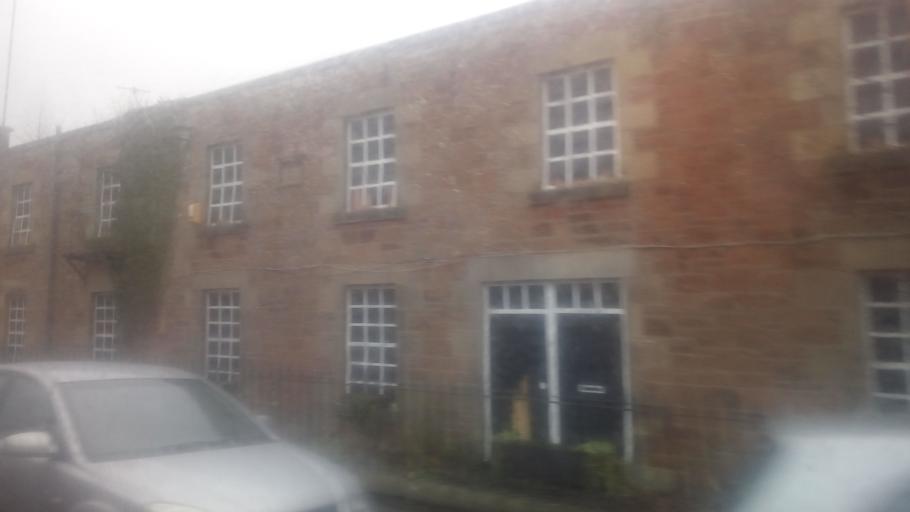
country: GB
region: Scotland
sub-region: The Scottish Borders
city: Newtown St Boswells
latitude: 55.5794
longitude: -2.6739
